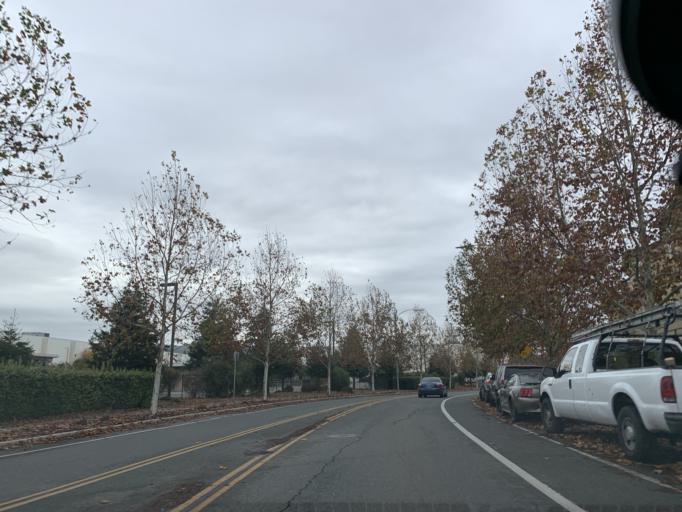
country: US
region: California
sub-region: Santa Clara County
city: Seven Trees
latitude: 37.2459
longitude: -121.7992
